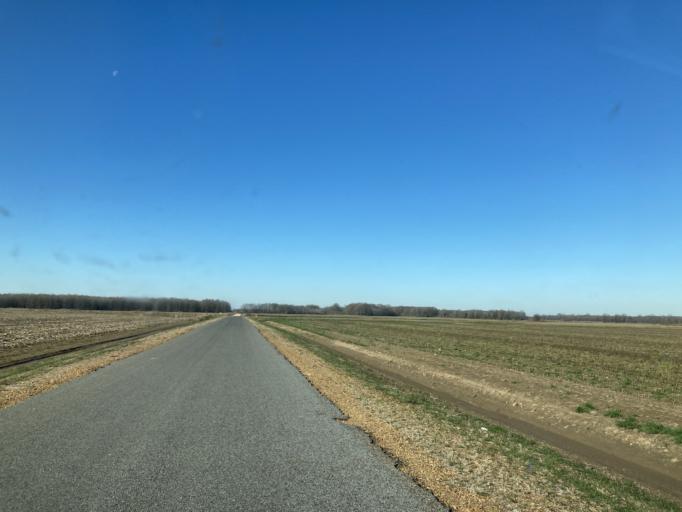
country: US
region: Mississippi
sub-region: Yazoo County
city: Yazoo City
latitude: 32.9519
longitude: -90.6031
